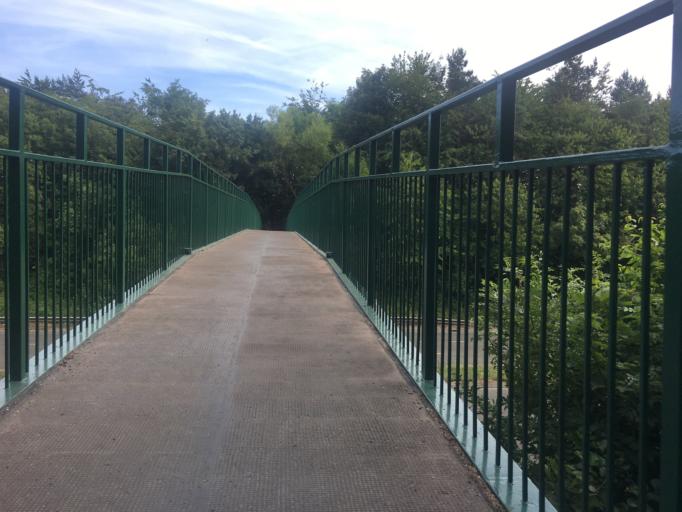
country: GB
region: England
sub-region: Sunderland
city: Washington
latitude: 54.8874
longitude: -1.5438
